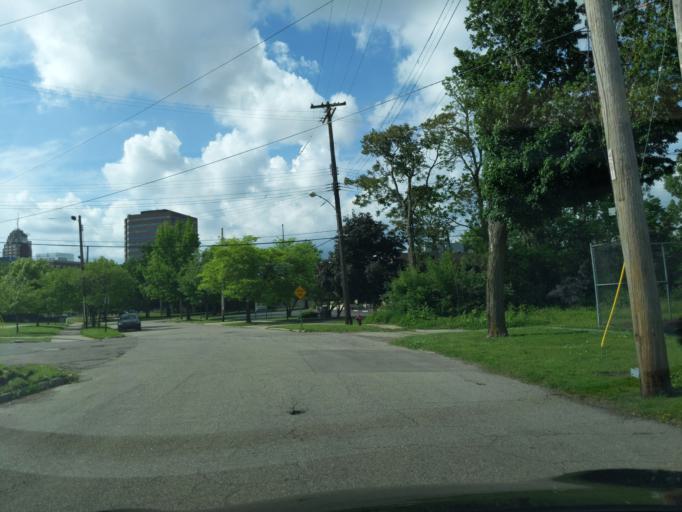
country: US
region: Michigan
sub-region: Ingham County
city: Lansing
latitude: 42.7284
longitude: -84.5475
